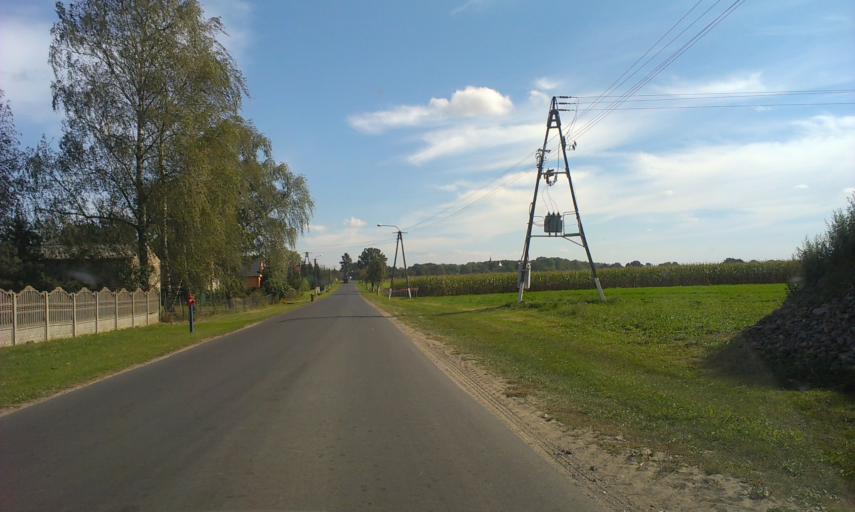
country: PL
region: Greater Poland Voivodeship
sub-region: Powiat pilski
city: Lobzenica
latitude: 53.2758
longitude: 17.2231
